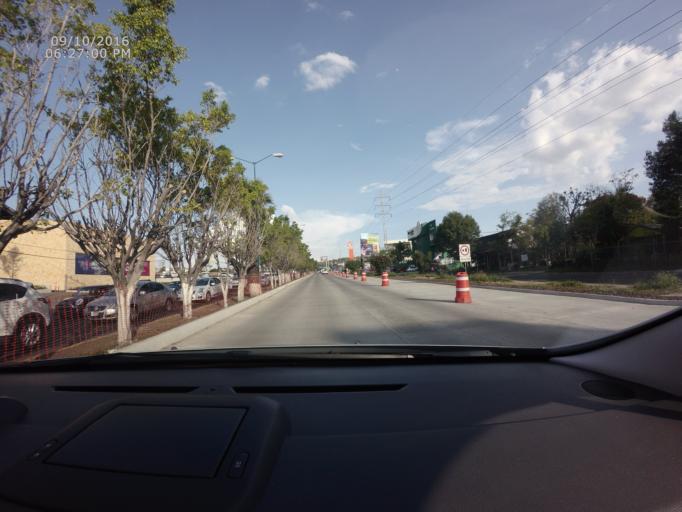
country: MX
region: Michoacan
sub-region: Morelia
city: Morelos
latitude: 19.6739
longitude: -101.2136
